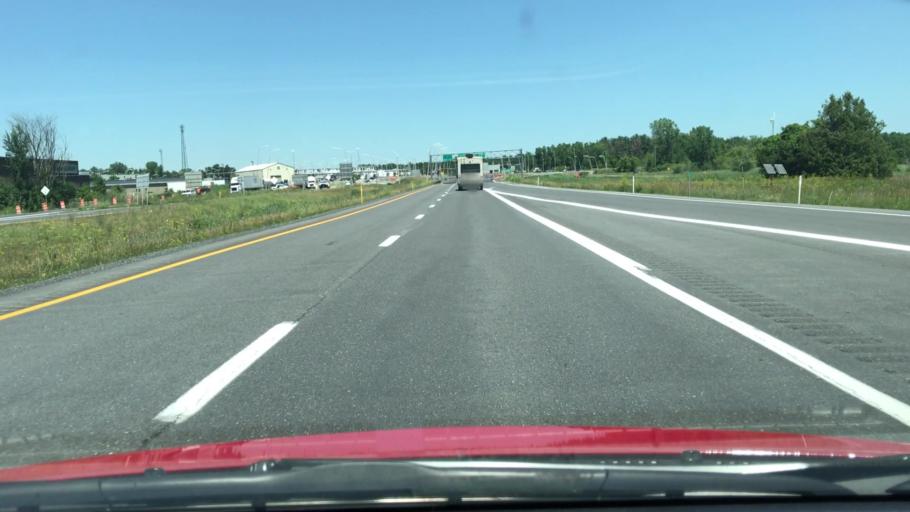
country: US
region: New York
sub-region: Clinton County
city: Champlain
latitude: 45.0010
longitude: -73.4540
